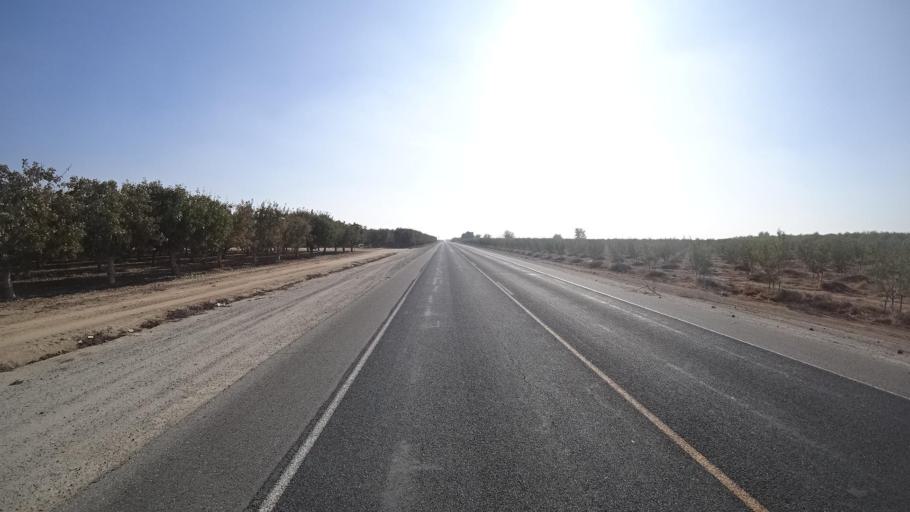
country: US
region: California
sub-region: Kern County
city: McFarland
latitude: 35.6558
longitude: -119.1957
